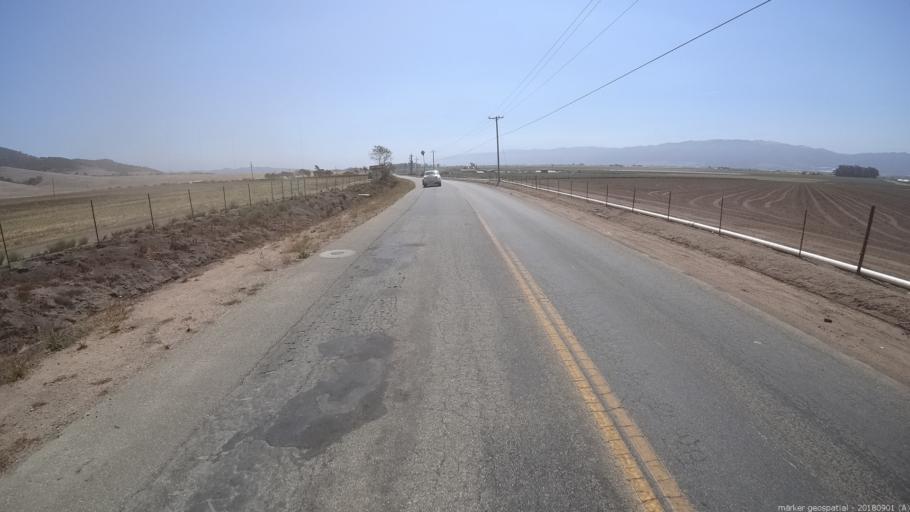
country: US
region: California
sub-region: Monterey County
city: Chualar
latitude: 36.6645
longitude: -121.5495
